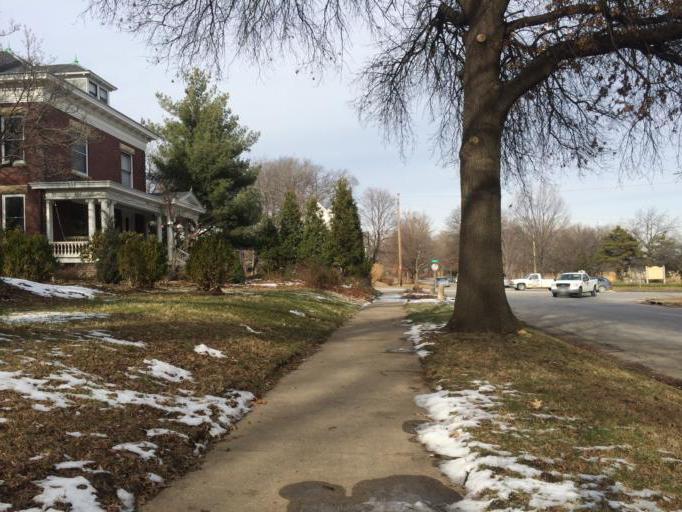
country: US
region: Kansas
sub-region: Douglas County
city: Lawrence
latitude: 38.9726
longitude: -95.2396
